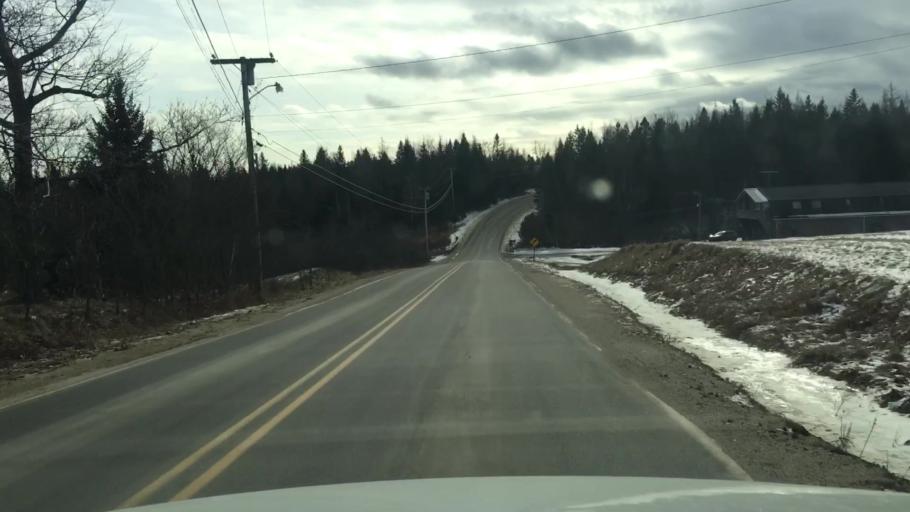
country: US
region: Maine
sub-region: Washington County
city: Jonesport
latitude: 44.6296
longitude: -67.5963
